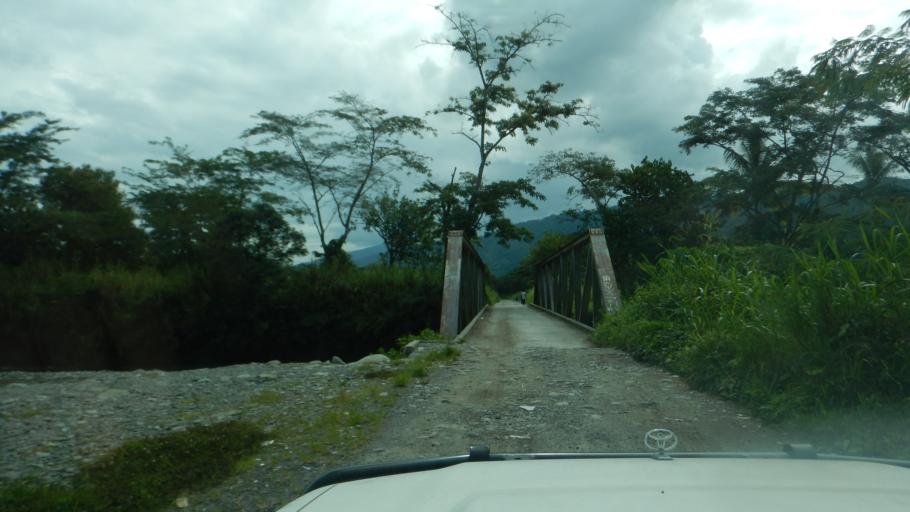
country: PG
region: Northern Province
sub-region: Sohe
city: Kokoda
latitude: -8.9056
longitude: 147.9689
